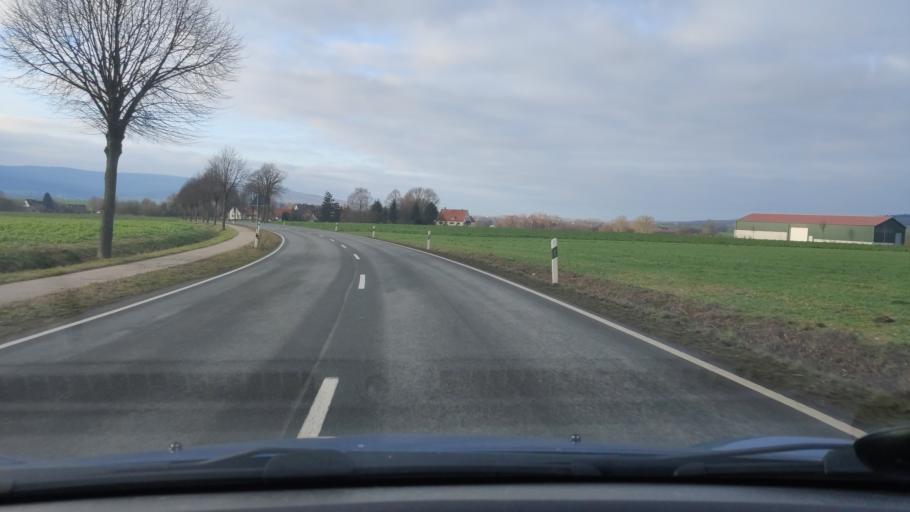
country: DE
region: Lower Saxony
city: Coppenbrugge
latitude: 52.1492
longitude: 9.5052
